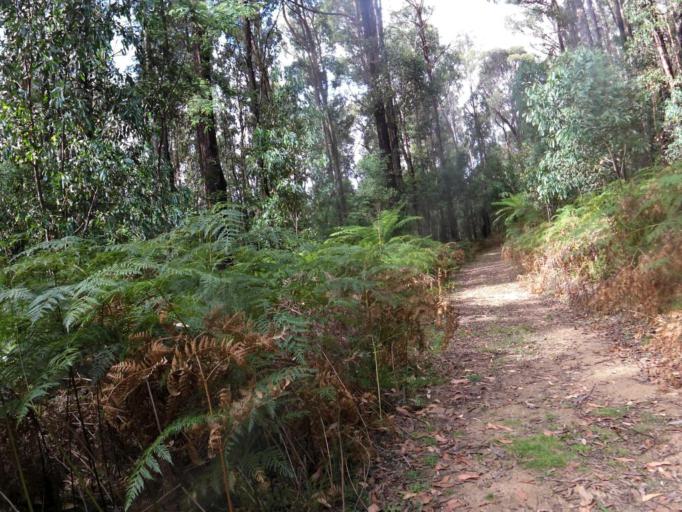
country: AU
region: Victoria
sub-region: Murrindindi
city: Alexandra
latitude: -37.3943
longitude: 145.5817
